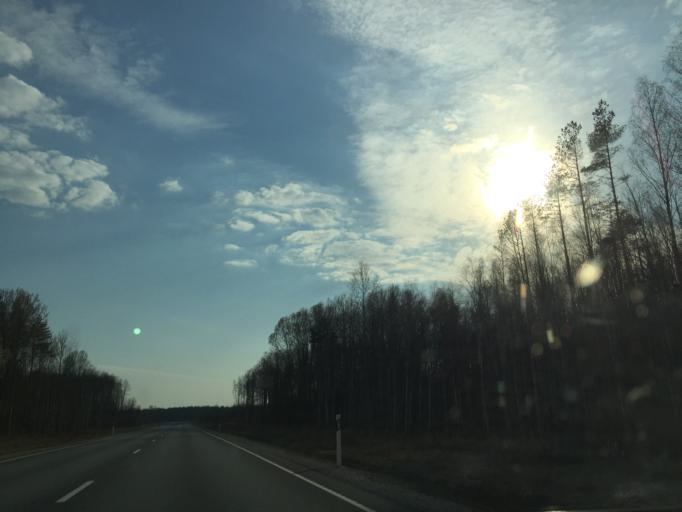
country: EE
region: Jogevamaa
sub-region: Mustvee linn
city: Mustvee
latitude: 58.8599
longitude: 26.9257
